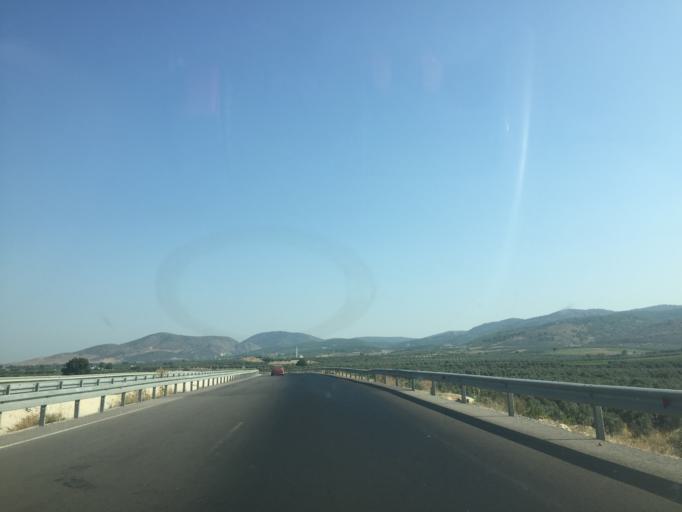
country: TR
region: Manisa
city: Golmarmara
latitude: 38.7801
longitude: 27.9049
